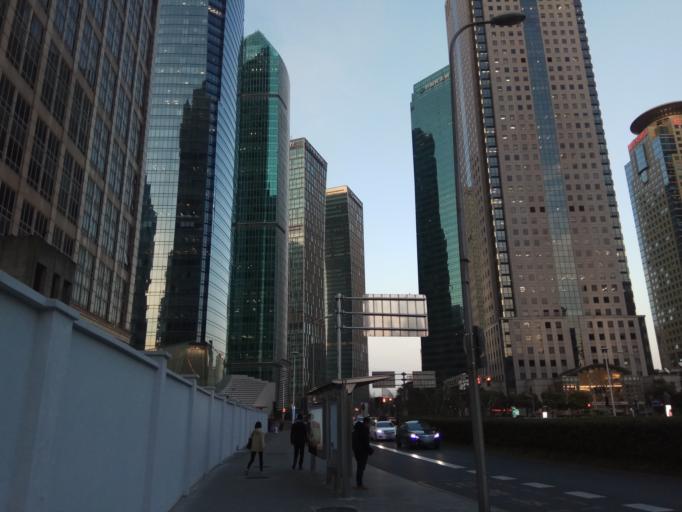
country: CN
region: Shanghai Shi
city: Hongkou
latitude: 31.2418
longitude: 121.5009
